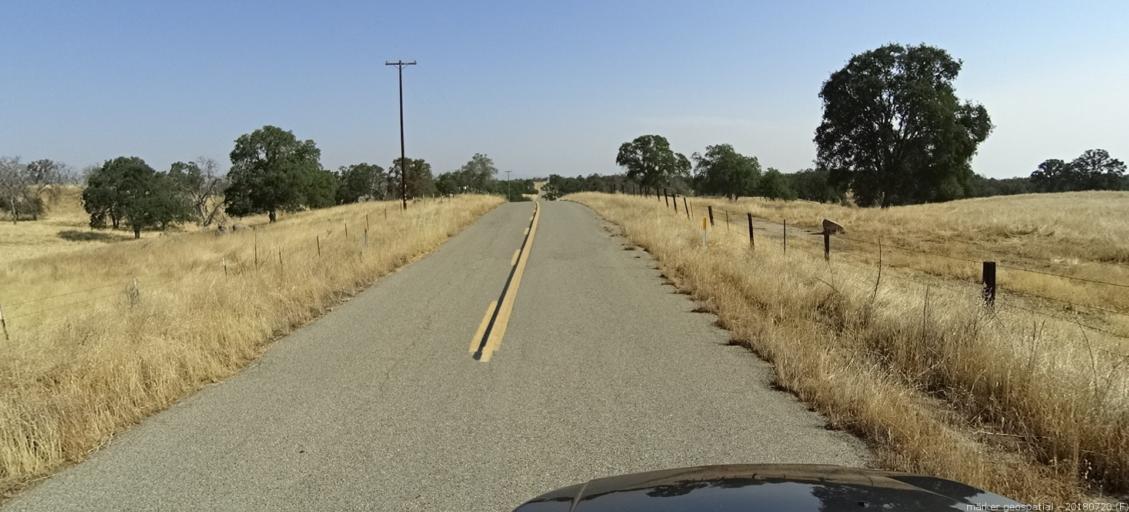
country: US
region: California
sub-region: Madera County
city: Yosemite Lakes
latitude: 37.2471
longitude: -119.9250
